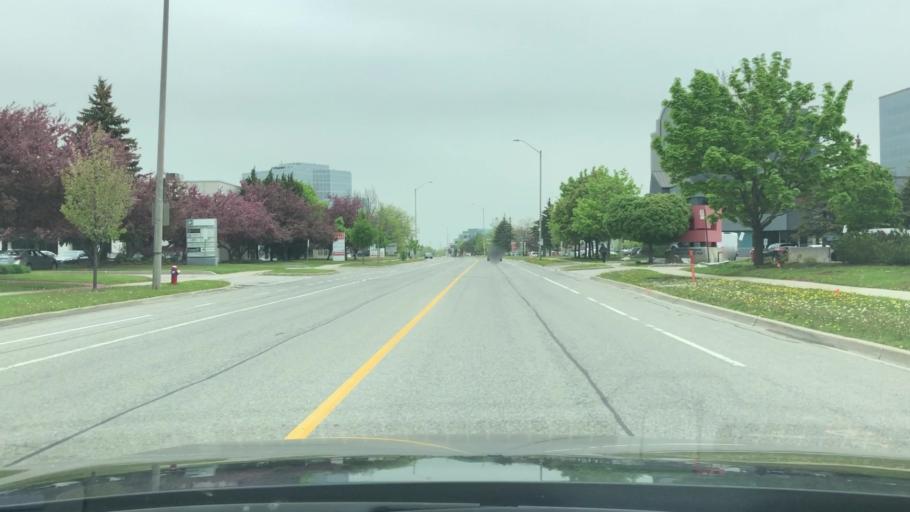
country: CA
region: Ontario
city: Etobicoke
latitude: 43.6580
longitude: -79.5993
